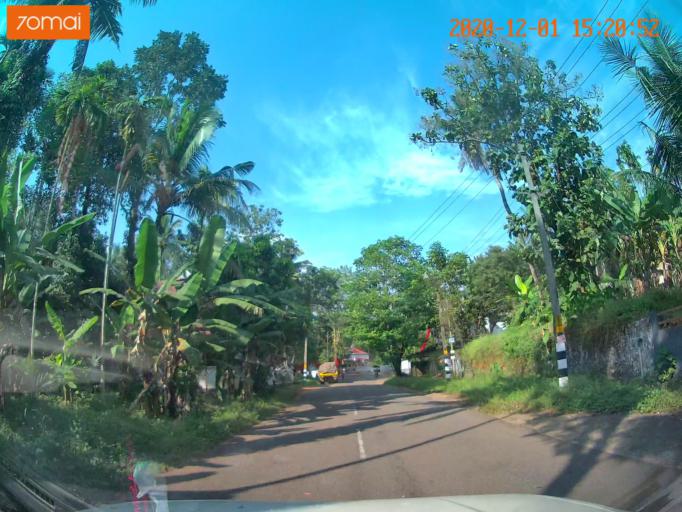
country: IN
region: Kerala
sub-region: Ernakulam
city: Ramamangalam
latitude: 9.9453
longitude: 76.5392
